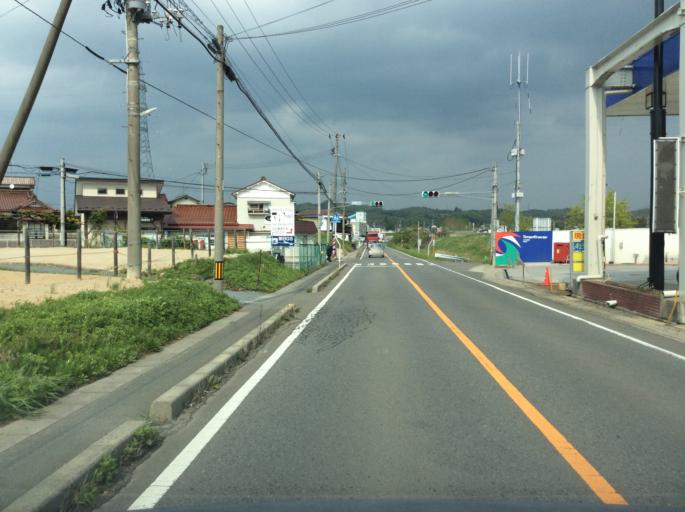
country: JP
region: Fukushima
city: Koriyama
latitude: 37.4204
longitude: 140.4081
